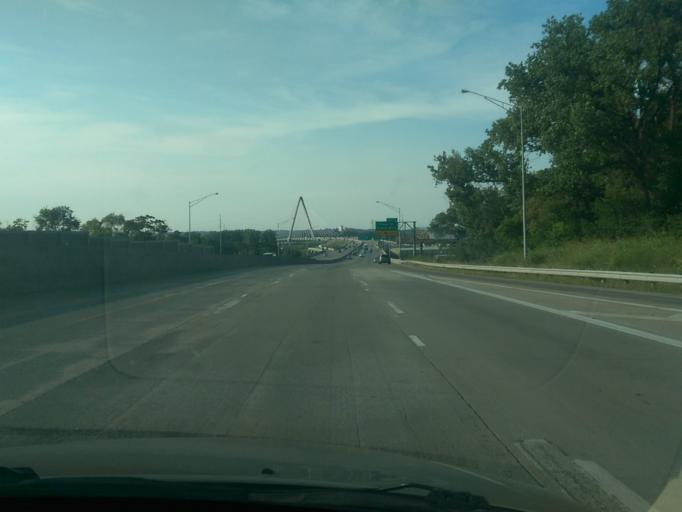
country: US
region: Missouri
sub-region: Clay County
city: North Kansas City
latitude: 39.1129
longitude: -94.5646
